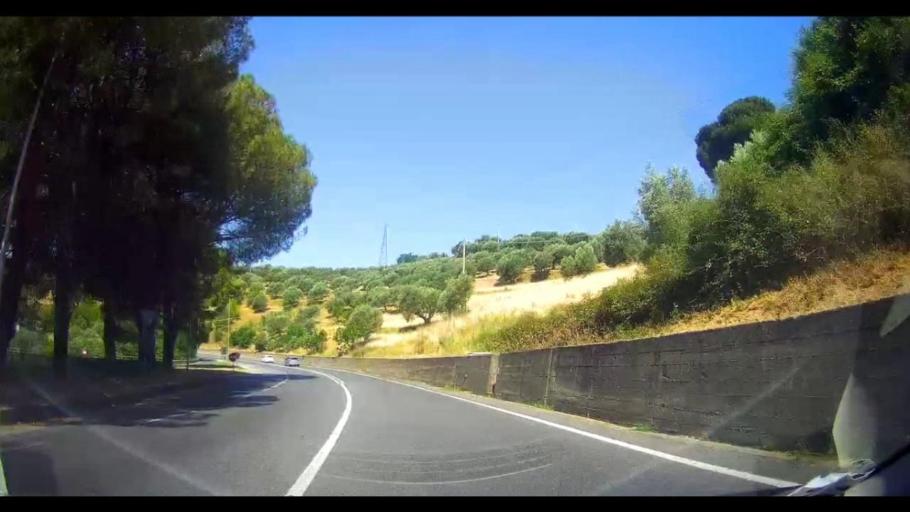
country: IT
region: Calabria
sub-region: Provincia di Cosenza
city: Cosenza
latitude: 39.2961
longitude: 16.2694
